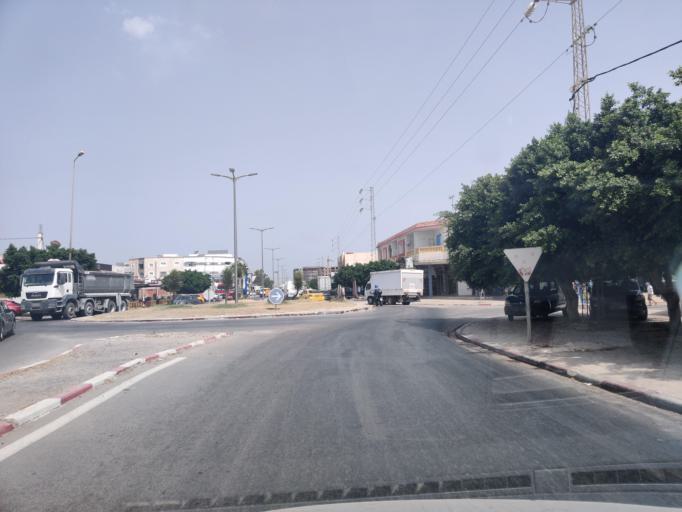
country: TN
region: Nabul
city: Bu `Urqub
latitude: 36.5900
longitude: 10.5048
